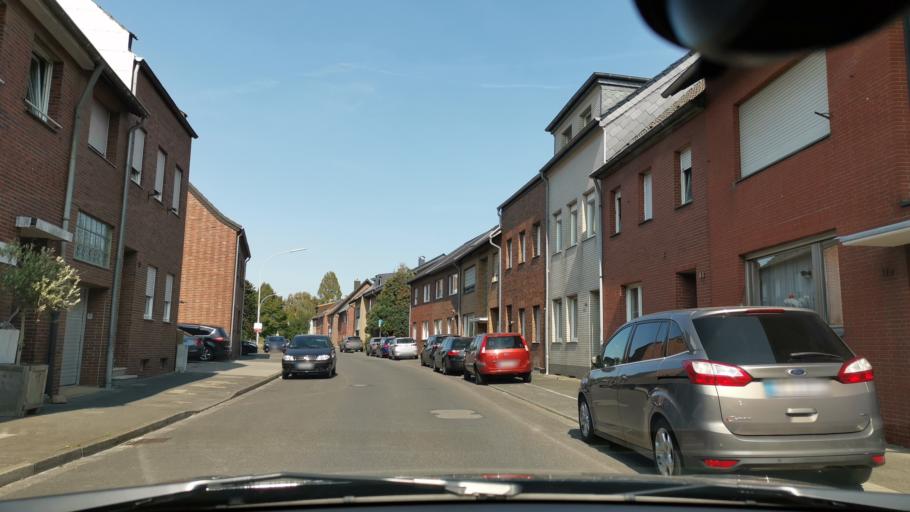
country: DE
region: North Rhine-Westphalia
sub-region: Regierungsbezirk Dusseldorf
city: Grevenbroich
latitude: 51.0749
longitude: 6.5677
